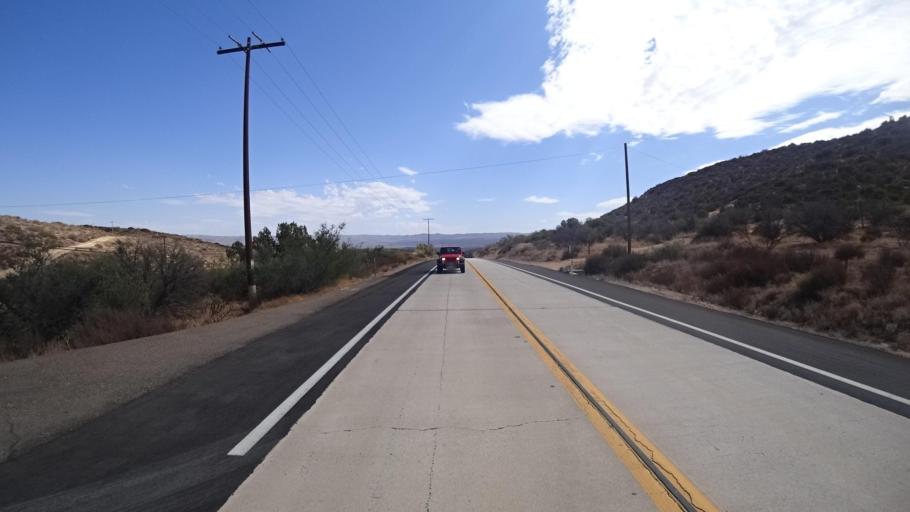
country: MX
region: Baja California
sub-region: Tecate
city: Cereso del Hongo
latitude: 32.6387
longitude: -116.2280
